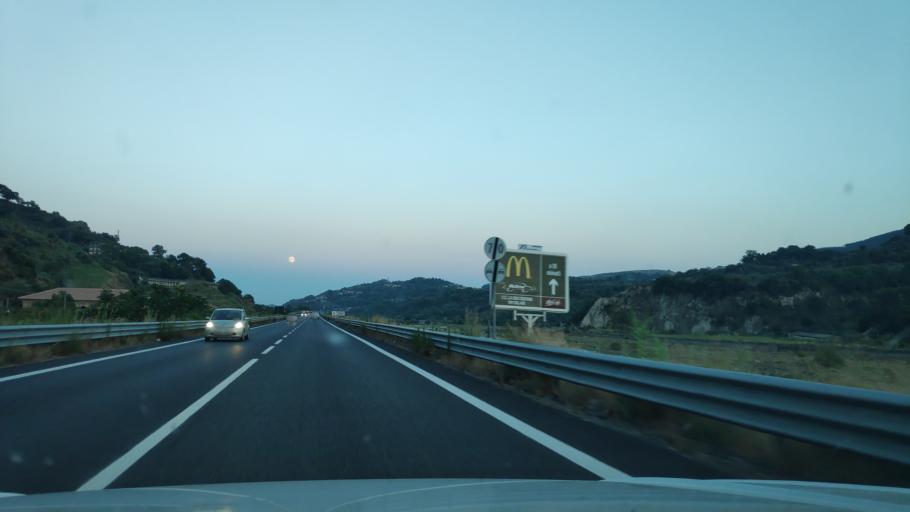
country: IT
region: Calabria
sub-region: Provincia di Reggio Calabria
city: Mammola
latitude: 38.3544
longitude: 16.2433
